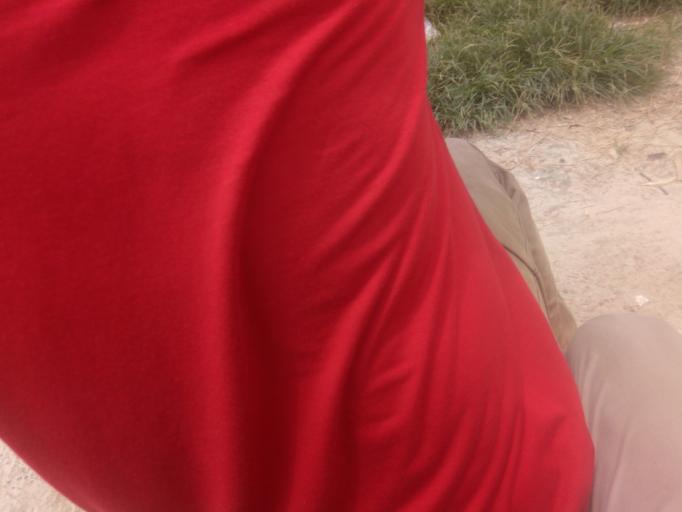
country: BD
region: Dhaka
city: Azimpur
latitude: 23.7553
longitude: 90.3465
